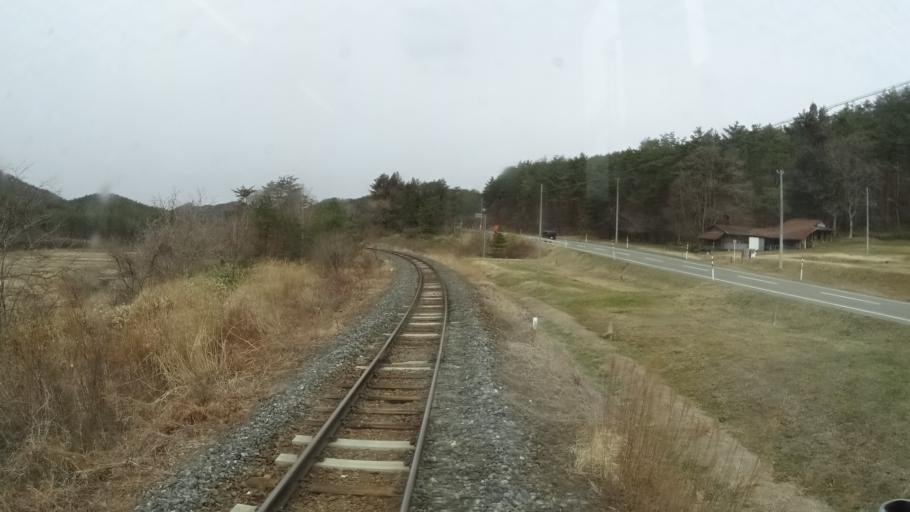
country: JP
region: Iwate
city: Tono
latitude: 39.3312
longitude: 141.3631
